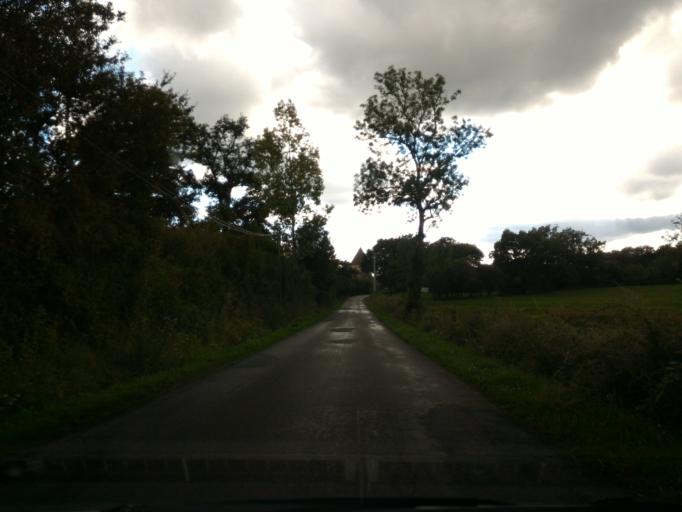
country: FR
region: Poitou-Charentes
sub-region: Departement de la Charente
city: Etagnac
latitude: 45.9515
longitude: 0.7887
